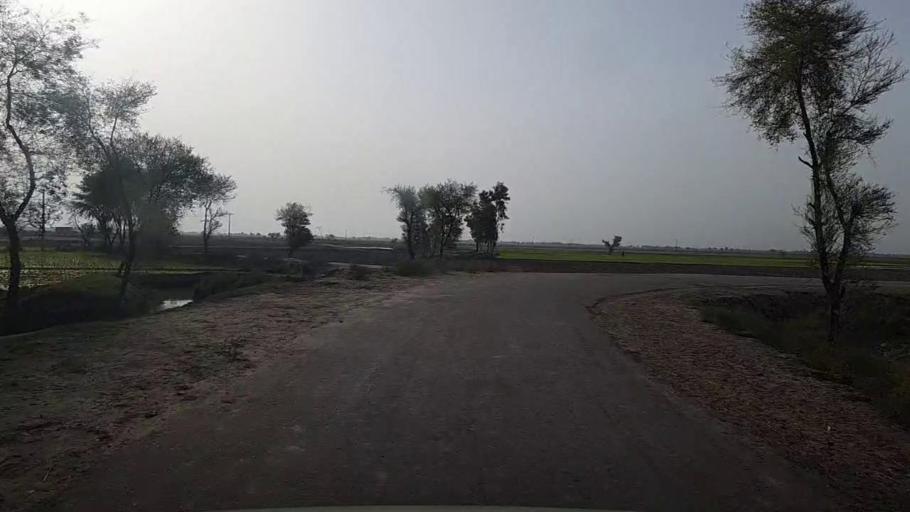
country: PK
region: Sindh
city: Khairpur Nathan Shah
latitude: 27.0953
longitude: 67.7955
